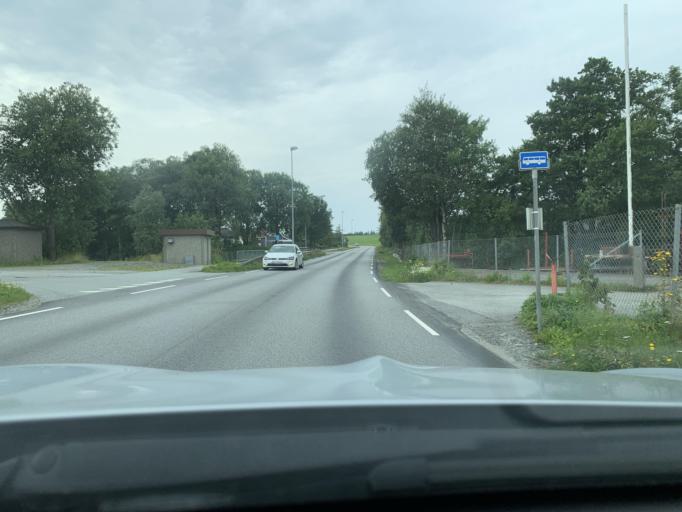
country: NO
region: Rogaland
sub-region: Time
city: Bryne
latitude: 58.7671
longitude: 5.7195
